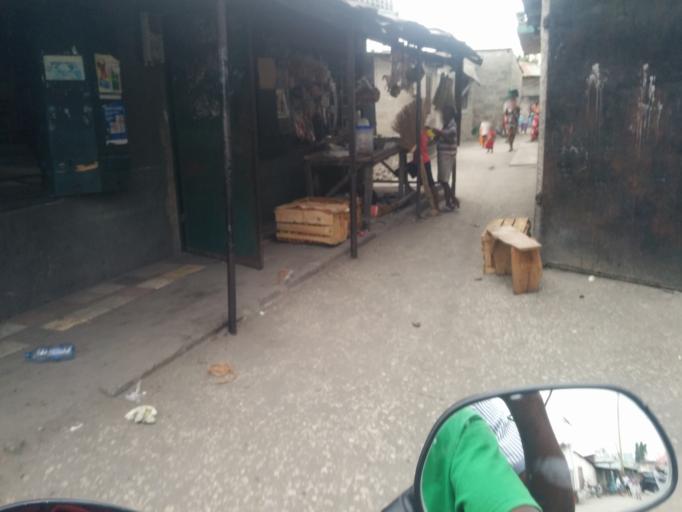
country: TZ
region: Dar es Salaam
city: Dar es Salaam
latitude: -6.8383
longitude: 39.2778
